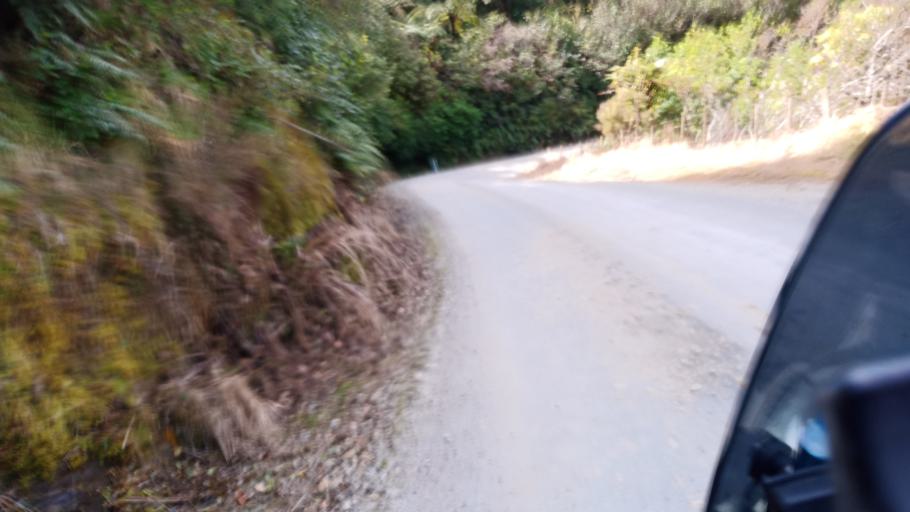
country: NZ
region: Gisborne
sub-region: Gisborne District
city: Gisborne
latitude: -38.8538
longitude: 177.7928
